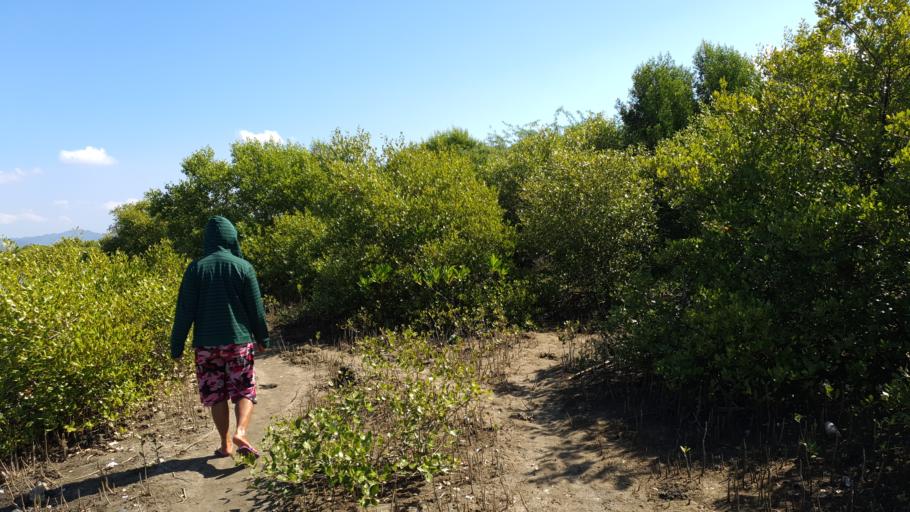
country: PH
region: Ilocos
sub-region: Province of La Union
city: Payocpoc Sur
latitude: 16.5032
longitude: 120.3074
